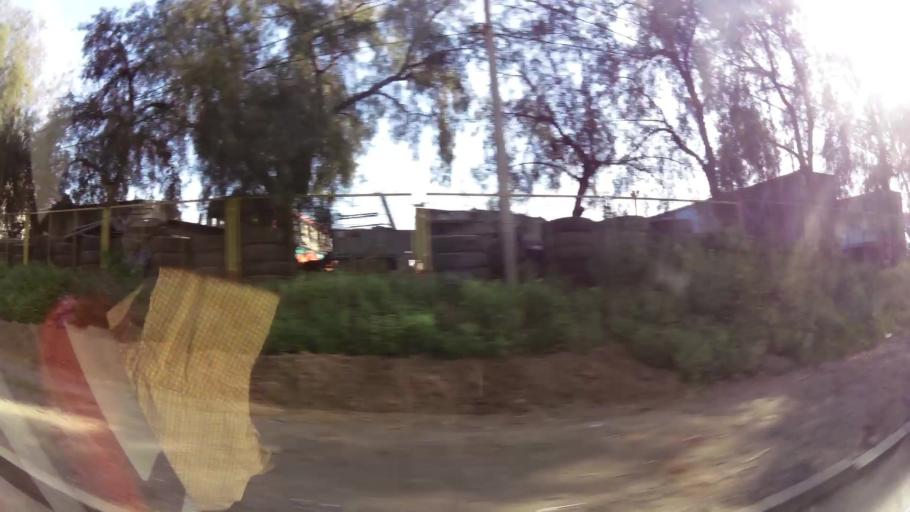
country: CL
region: Santiago Metropolitan
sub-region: Provincia de Santiago
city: Lo Prado
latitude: -33.4139
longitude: -70.7606
